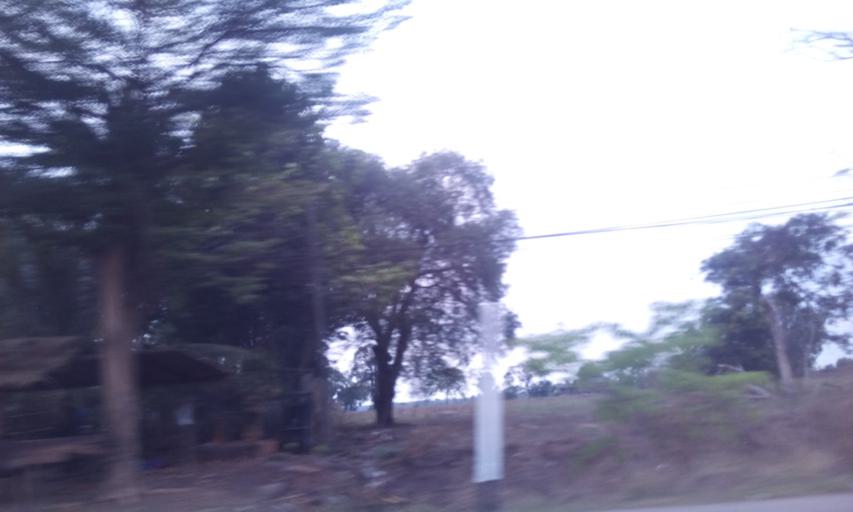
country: TH
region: Chanthaburi
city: Khlung
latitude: 12.4154
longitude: 102.3282
